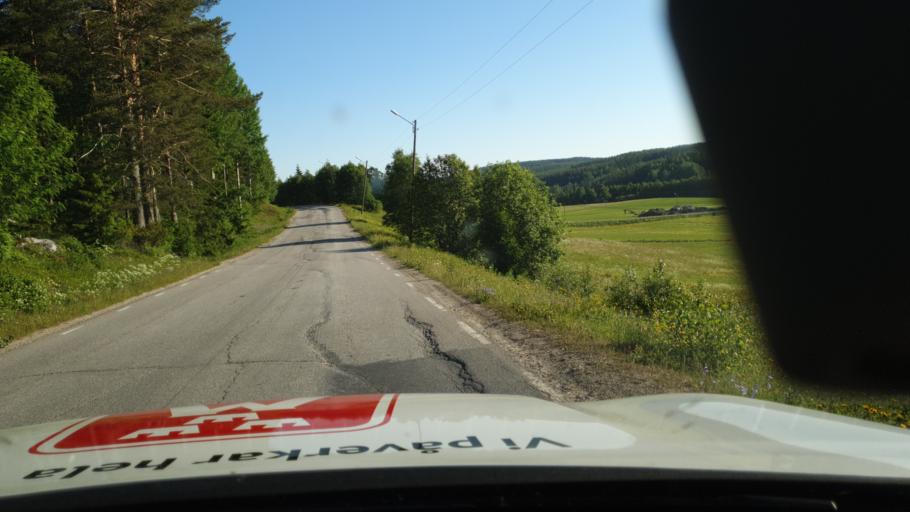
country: SE
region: Vaesterbotten
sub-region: Umea Kommun
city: Roback
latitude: 64.0305
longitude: 20.0842
